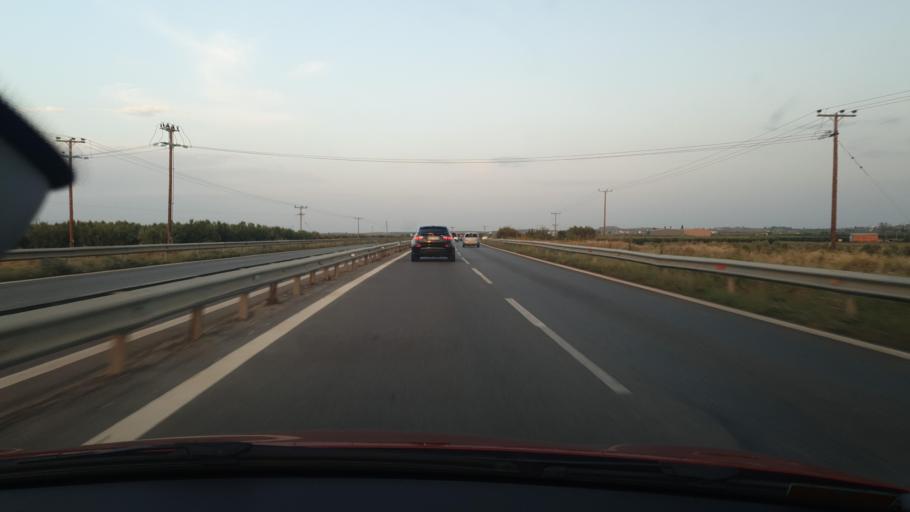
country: GR
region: Central Macedonia
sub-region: Nomos Chalkidikis
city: Nea Plagia
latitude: 40.2845
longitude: 23.1809
